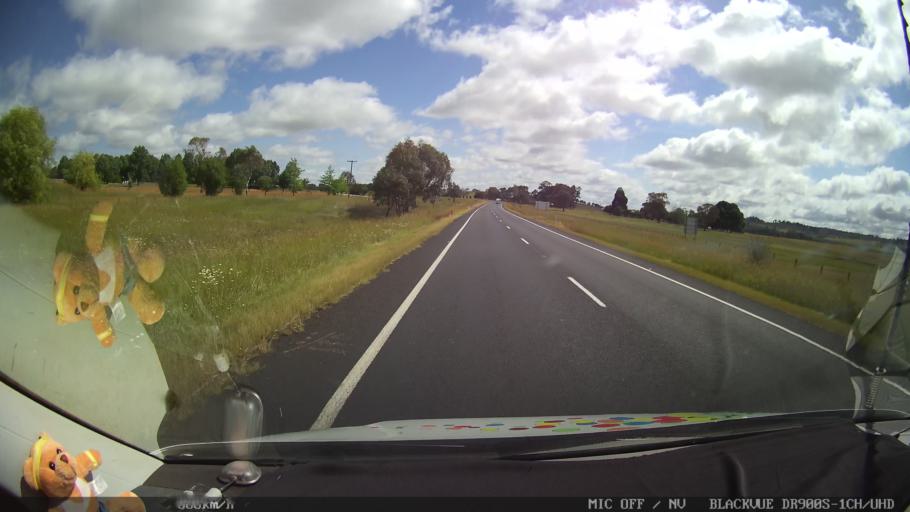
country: AU
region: New South Wales
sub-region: Glen Innes Severn
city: Glen Innes
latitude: -29.9141
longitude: 151.7294
